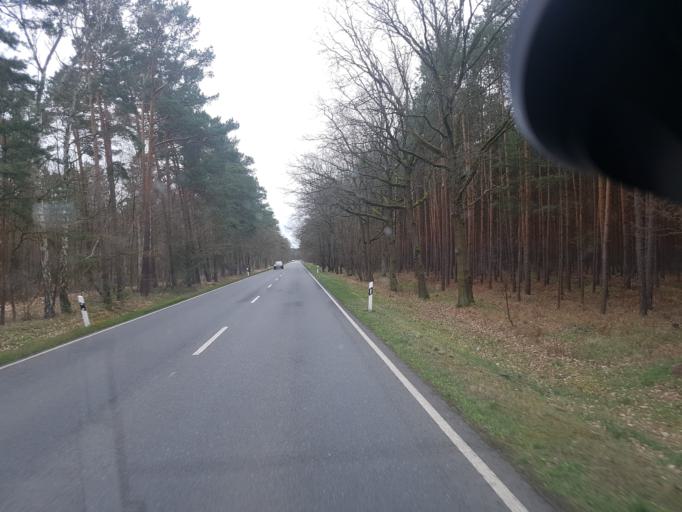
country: DE
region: Brandenburg
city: Luebben
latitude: 51.9684
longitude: 13.9499
